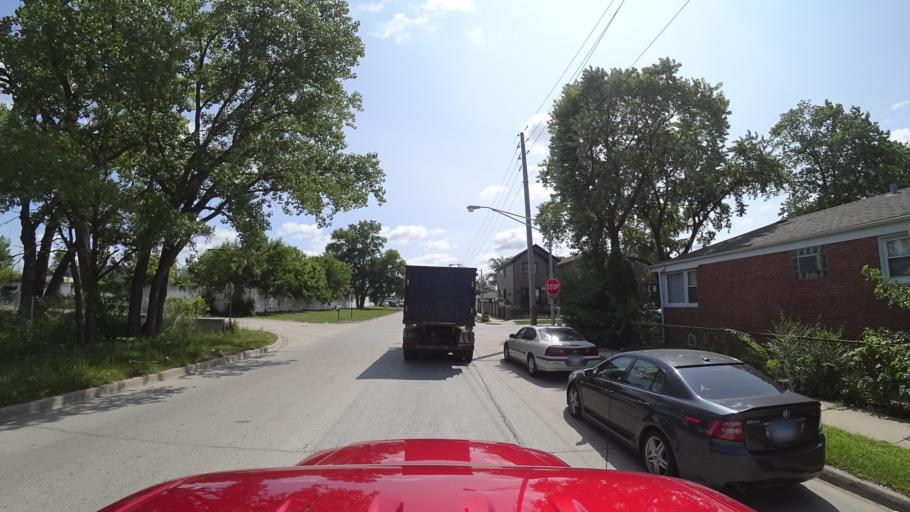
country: US
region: Illinois
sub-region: Cook County
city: Cicero
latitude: 41.8150
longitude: -87.7426
